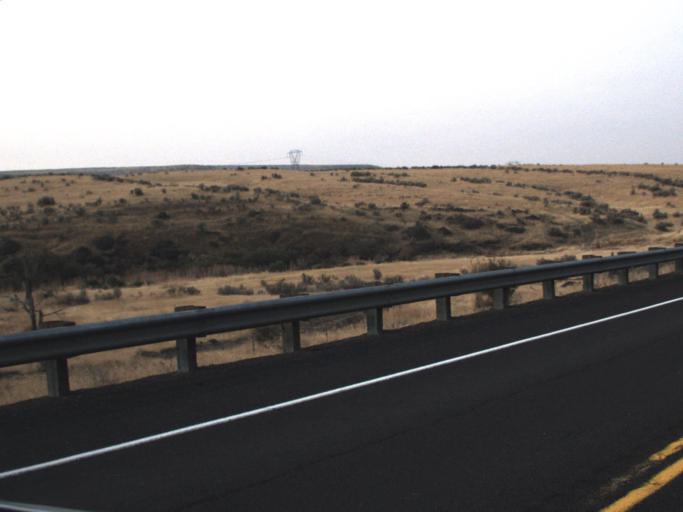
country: US
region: Washington
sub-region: Yakima County
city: Toppenish
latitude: 46.2537
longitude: -120.4122
